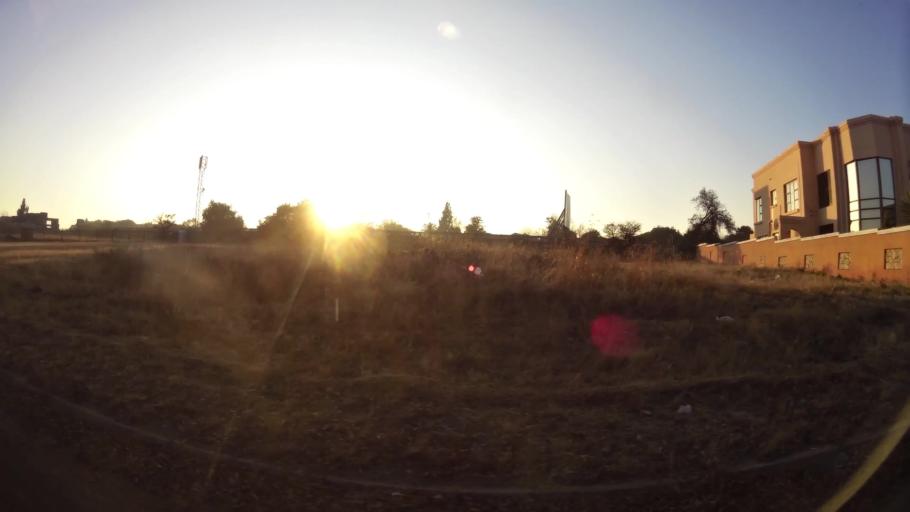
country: ZA
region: Orange Free State
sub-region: Mangaung Metropolitan Municipality
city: Bloemfontein
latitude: -29.1025
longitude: 26.1640
